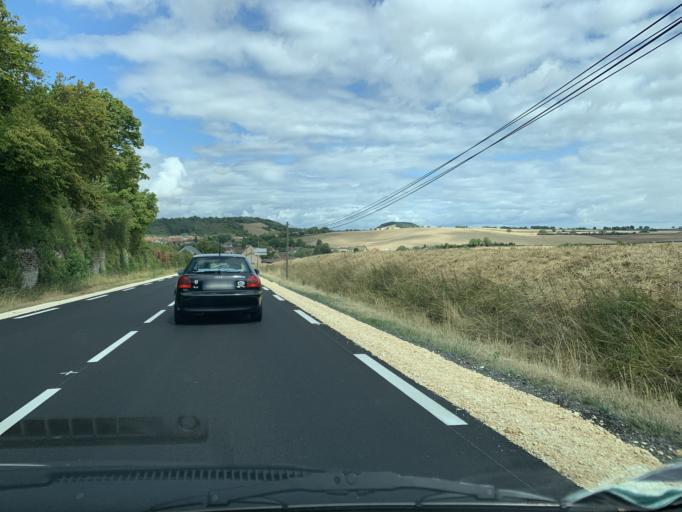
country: FR
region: Bourgogne
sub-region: Departement de la Nievre
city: Varzy
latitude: 47.3510
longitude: 3.3796
